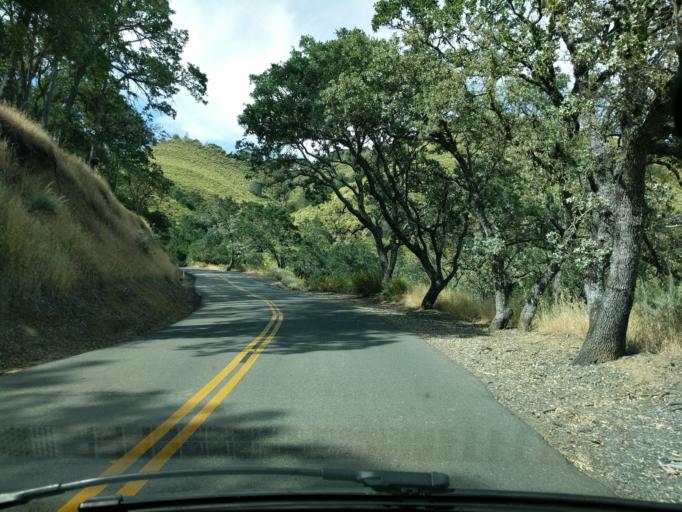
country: US
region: California
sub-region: Contra Costa County
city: Diablo
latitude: 37.8425
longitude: -121.9371
